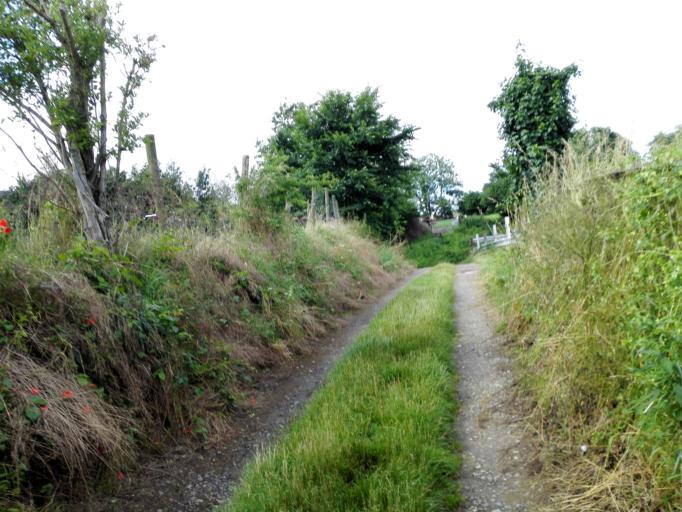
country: BE
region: Flanders
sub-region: Provincie Vlaams-Brabant
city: Bertem
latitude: 50.8659
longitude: 4.6434
